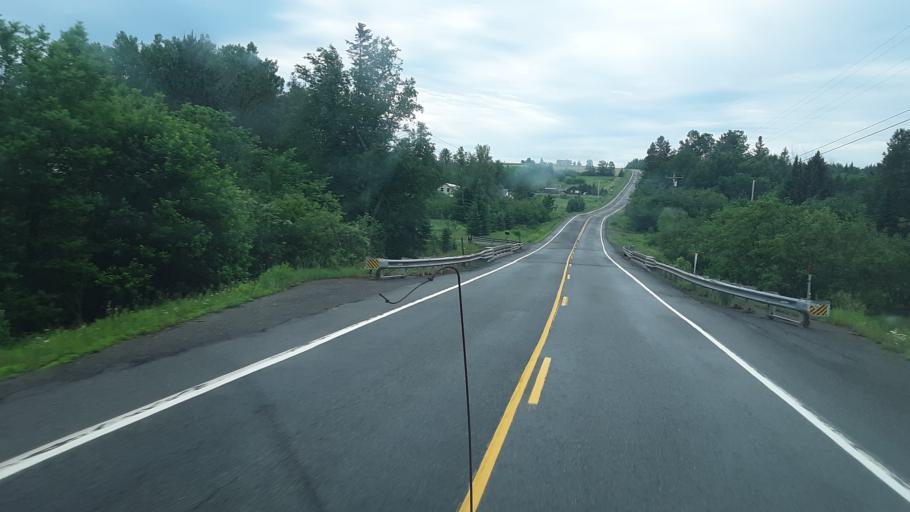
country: US
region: Maine
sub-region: Penobscot County
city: Patten
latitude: 46.0542
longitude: -68.4418
